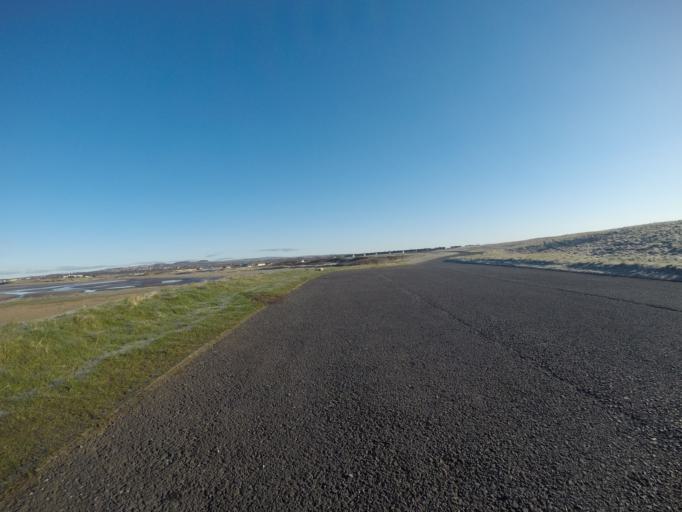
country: GB
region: Scotland
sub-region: North Ayrshire
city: Stevenston
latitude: 55.6261
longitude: -4.7495
